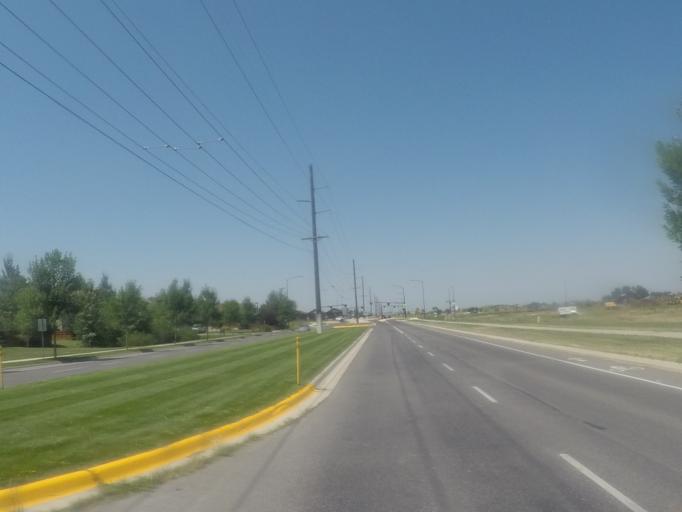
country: US
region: Montana
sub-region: Gallatin County
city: Bozeman
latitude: 45.6930
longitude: -111.0797
